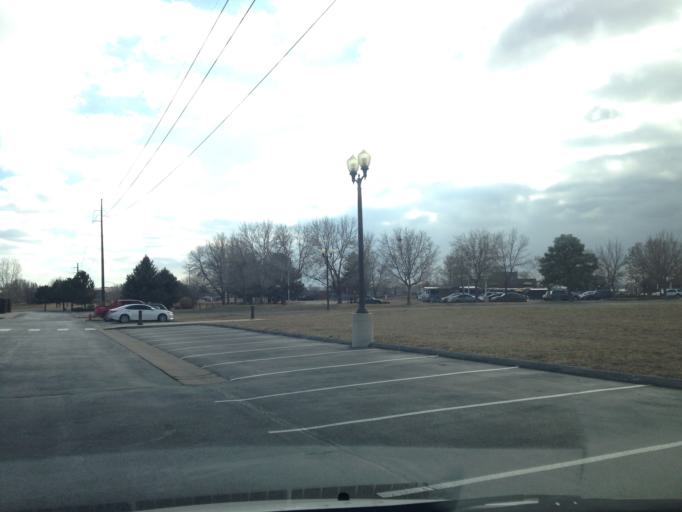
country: US
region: Colorado
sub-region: Boulder County
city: Lafayette
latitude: 39.9900
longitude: -105.0895
